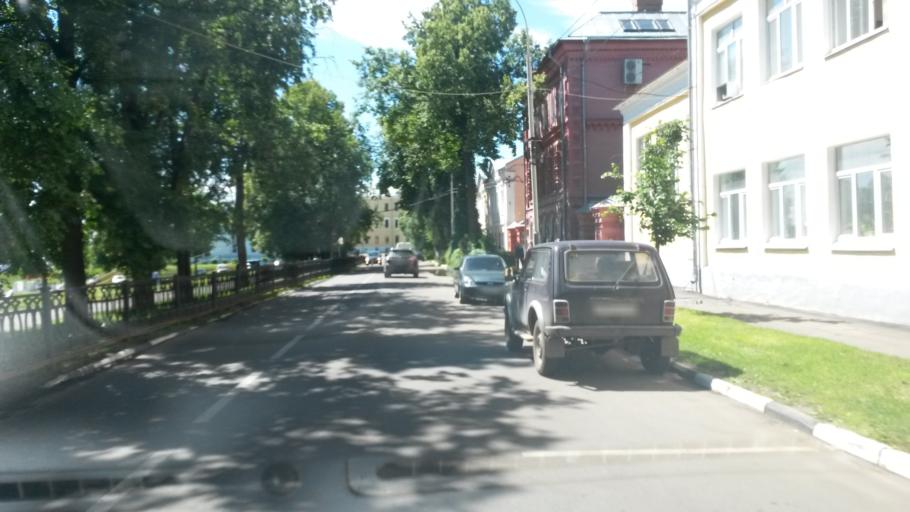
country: RU
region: Jaroslavl
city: Yaroslavl
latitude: 57.6238
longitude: 39.8979
